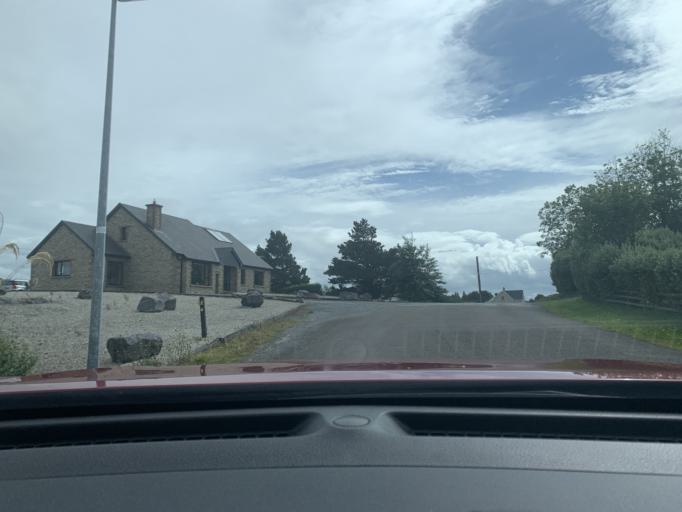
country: IE
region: Ulster
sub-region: County Donegal
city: Dungloe
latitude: 54.9439
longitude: -8.3581
